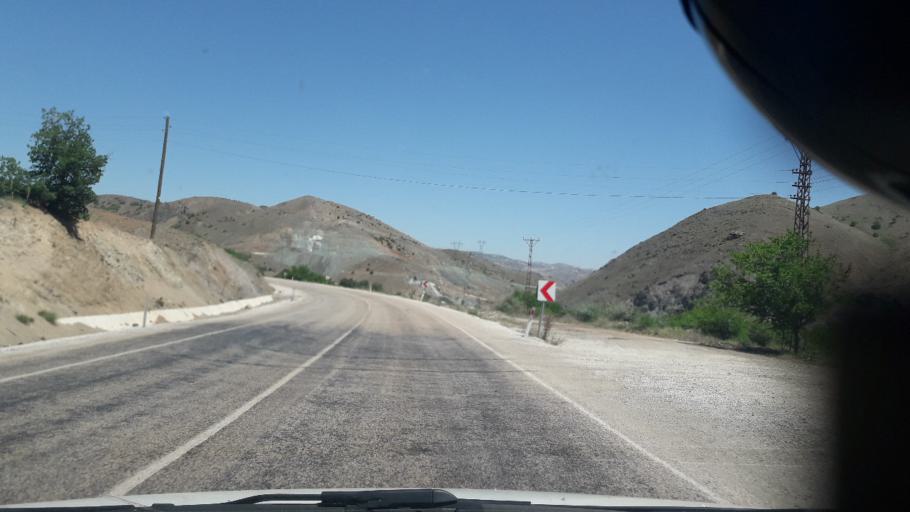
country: TR
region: Malatya
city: Hekimhan
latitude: 38.8272
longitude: 37.8572
